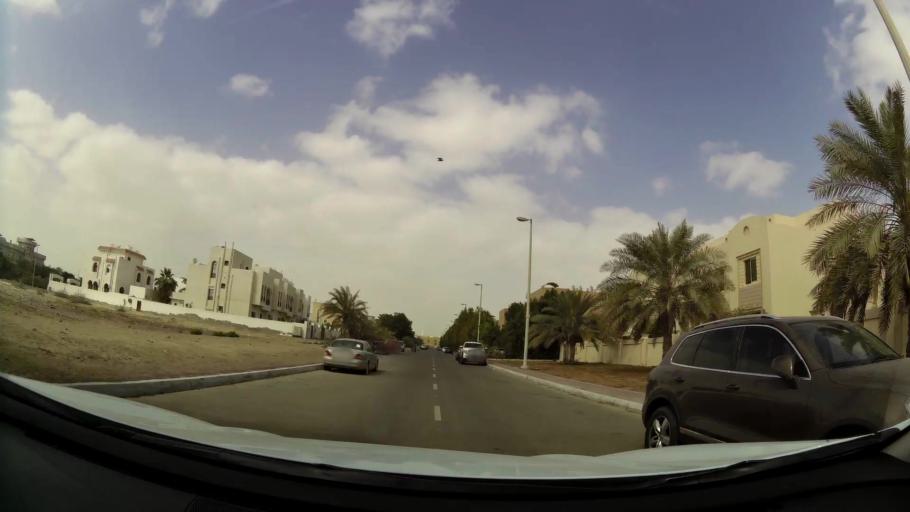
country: AE
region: Abu Dhabi
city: Abu Dhabi
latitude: 24.4071
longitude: 54.5004
